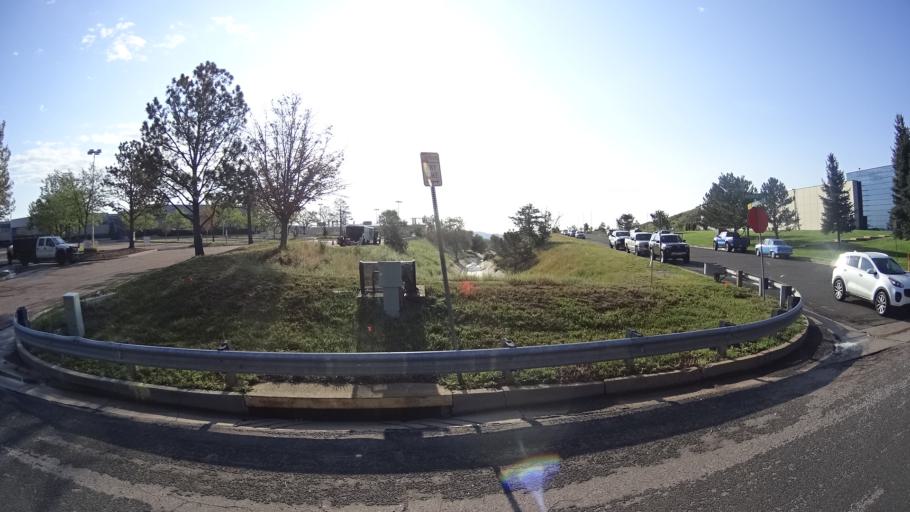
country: US
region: Colorado
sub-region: El Paso County
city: Manitou Springs
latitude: 38.8945
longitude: -104.8640
